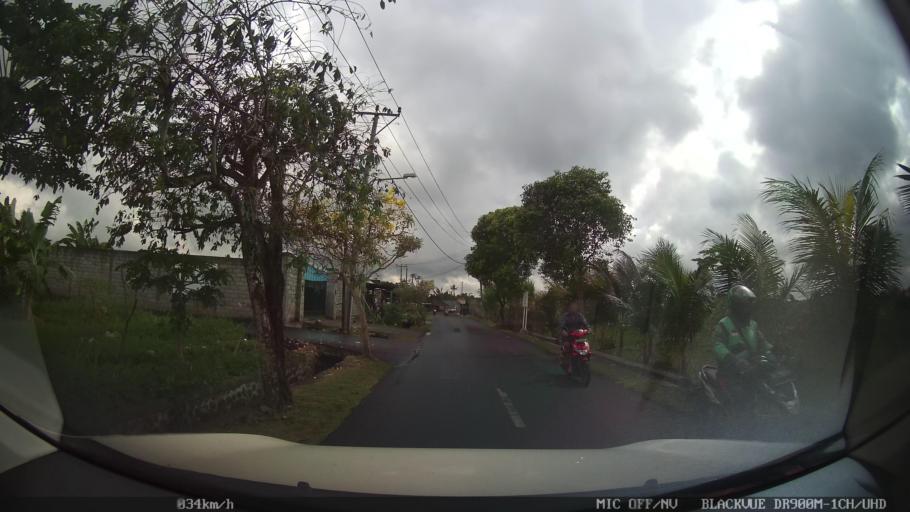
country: ID
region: Bali
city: Banjar Batur
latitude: -8.6026
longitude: 115.2060
